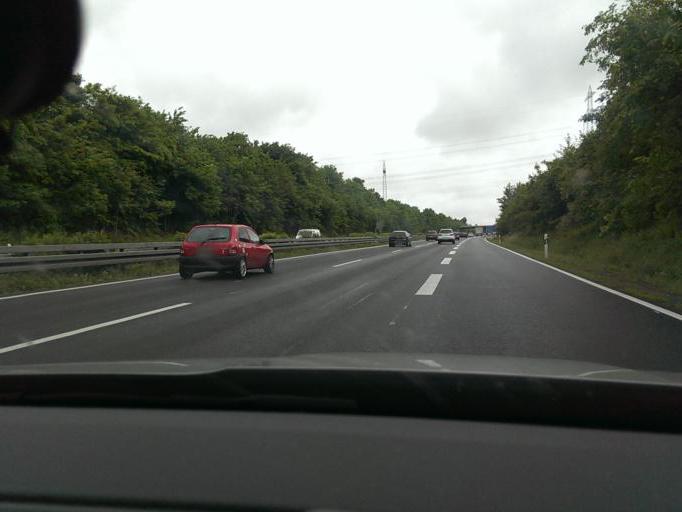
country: DE
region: Lower Saxony
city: Lehre
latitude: 52.3628
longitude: 10.7238
